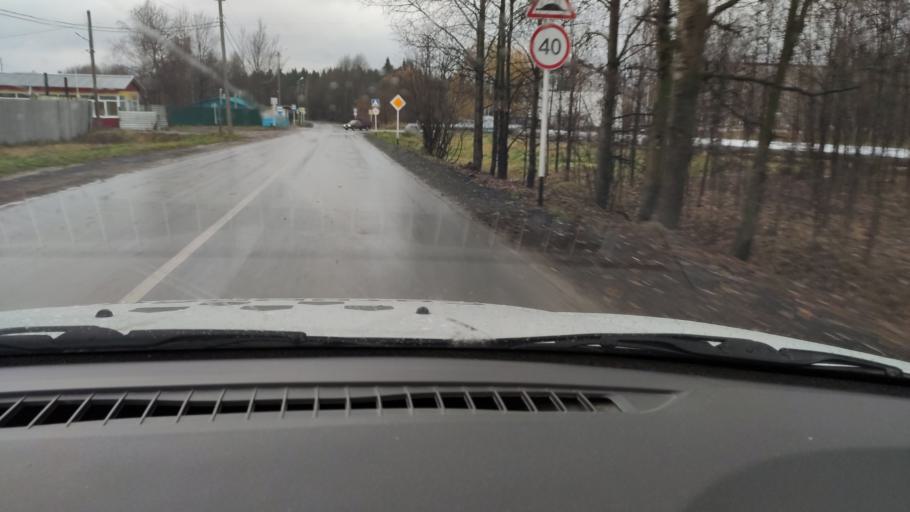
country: RU
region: Perm
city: Sylva
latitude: 58.0297
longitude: 56.7404
